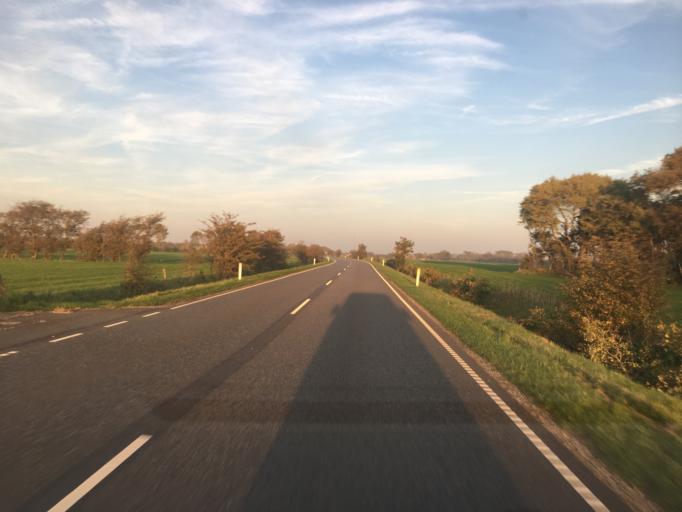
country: DK
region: South Denmark
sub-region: Tonder Kommune
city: Logumkloster
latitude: 55.0488
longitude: 9.0807
